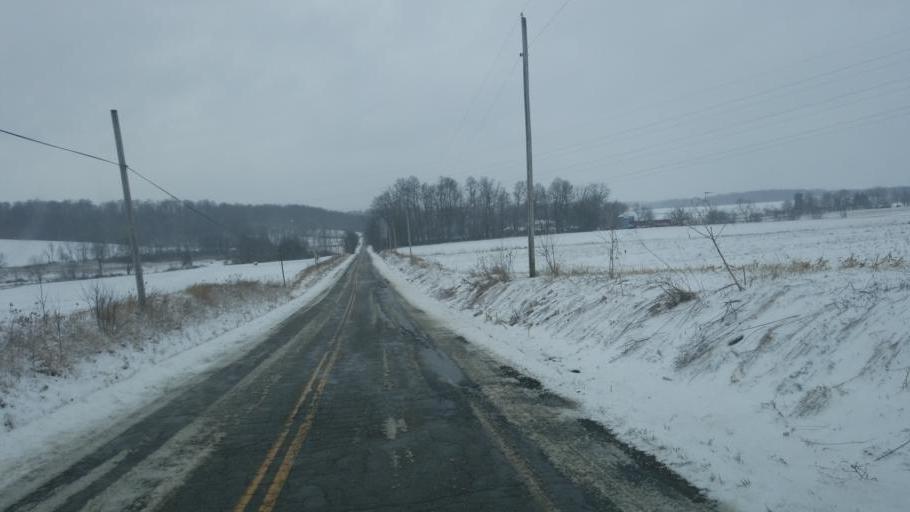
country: US
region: Ohio
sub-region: Sandusky County
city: Bellville
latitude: 40.5287
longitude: -82.4103
